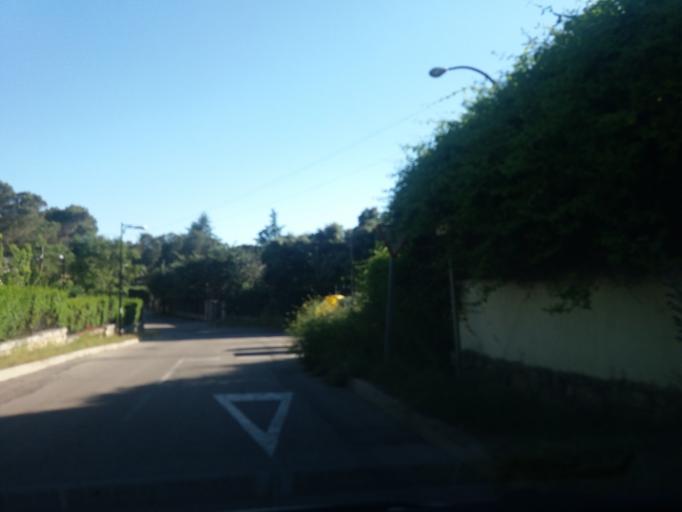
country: ES
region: Madrid
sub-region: Provincia de Madrid
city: Torrelodones
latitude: 40.5835
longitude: -3.9589
